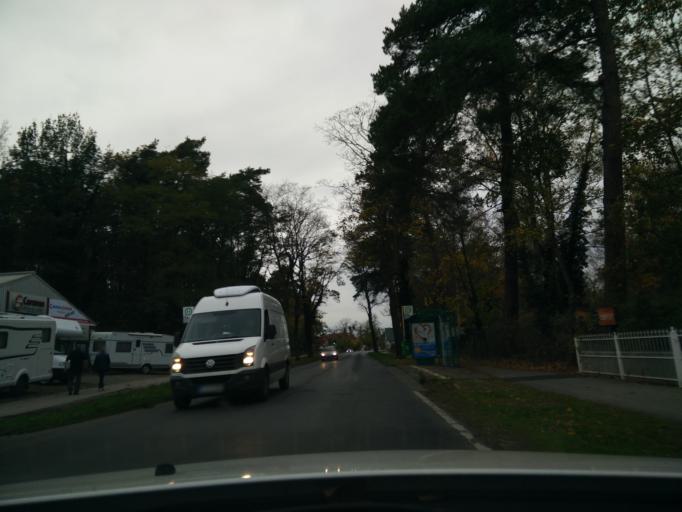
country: DE
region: Brandenburg
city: Falkensee
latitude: 52.5720
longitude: 13.0889
